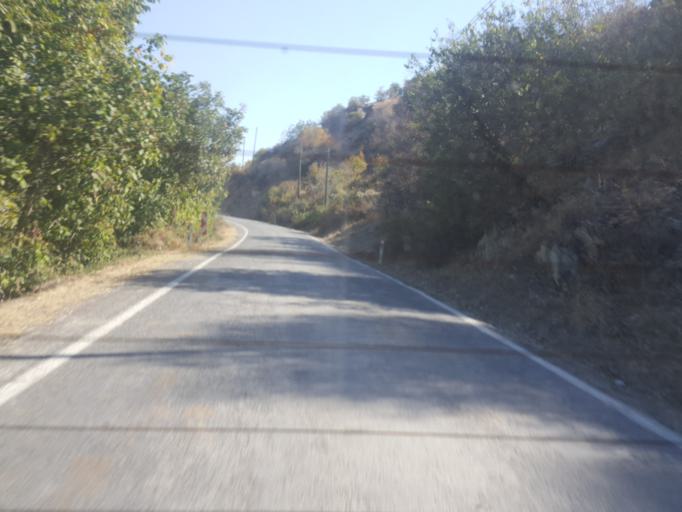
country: TR
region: Kastamonu
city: Tosya
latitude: 40.9854
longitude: 34.1032
